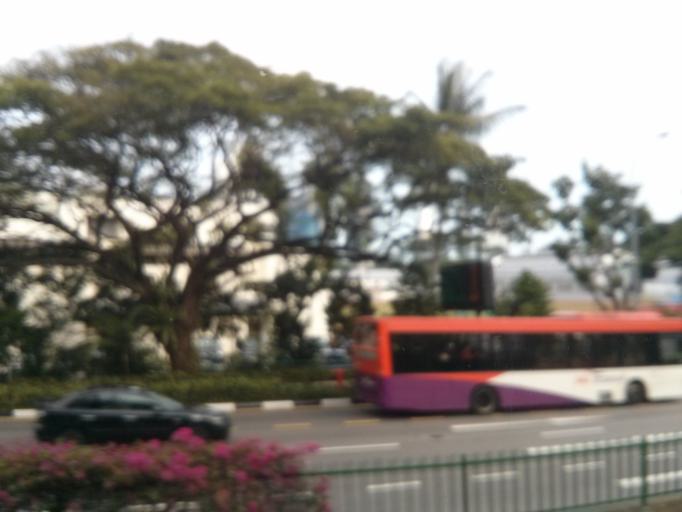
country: SG
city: Singapore
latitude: 1.2762
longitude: 103.8021
